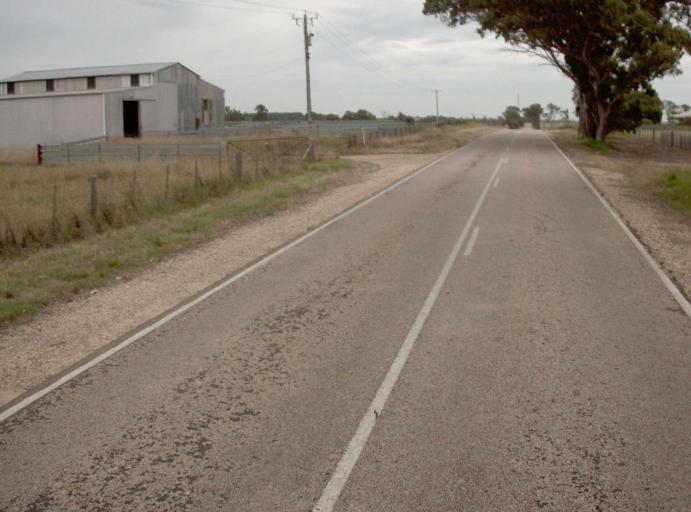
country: AU
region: Victoria
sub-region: East Gippsland
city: Bairnsdale
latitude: -37.8553
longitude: 147.4282
